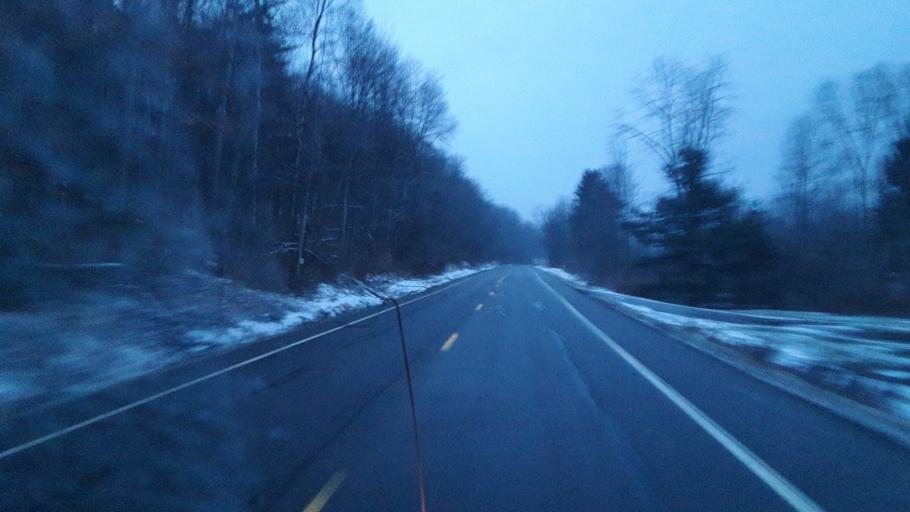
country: US
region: New York
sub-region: Allegany County
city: Belmont
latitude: 42.3171
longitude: -78.0981
